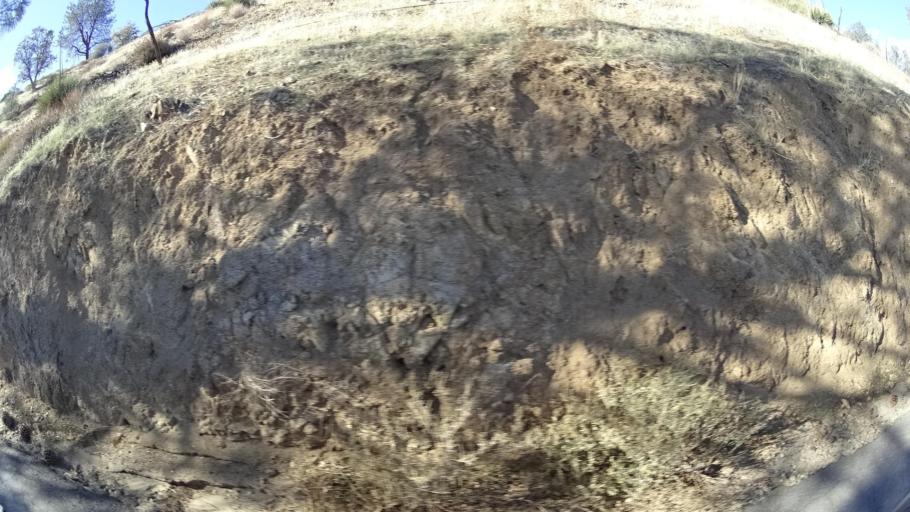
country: US
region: California
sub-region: Kern County
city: Bodfish
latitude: 35.5854
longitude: -118.5012
